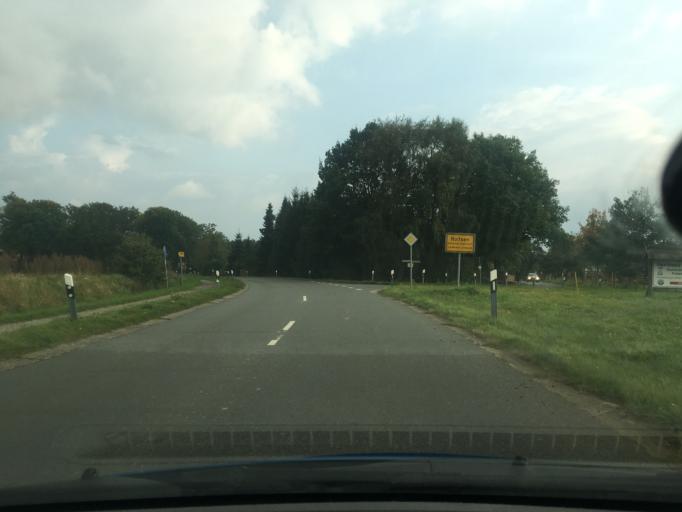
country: DE
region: Lower Saxony
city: Soderstorf
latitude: 53.1658
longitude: 10.1582
